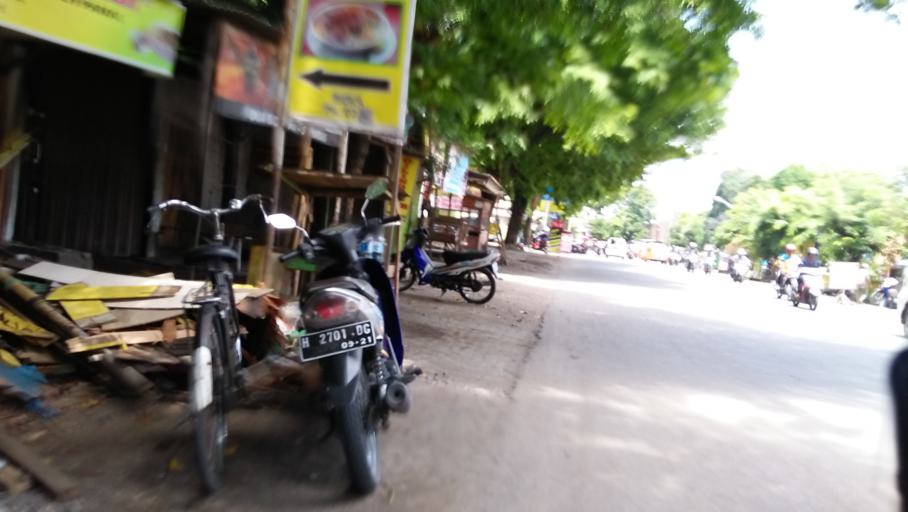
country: ID
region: Central Java
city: Mranggen
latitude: -7.0173
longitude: 110.4719
